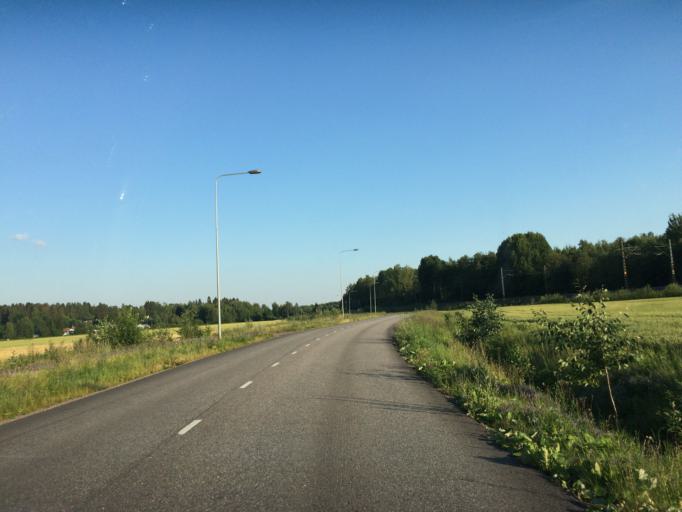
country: FI
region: Haeme
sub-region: Haemeenlinna
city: Parola
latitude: 61.0415
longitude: 24.3809
